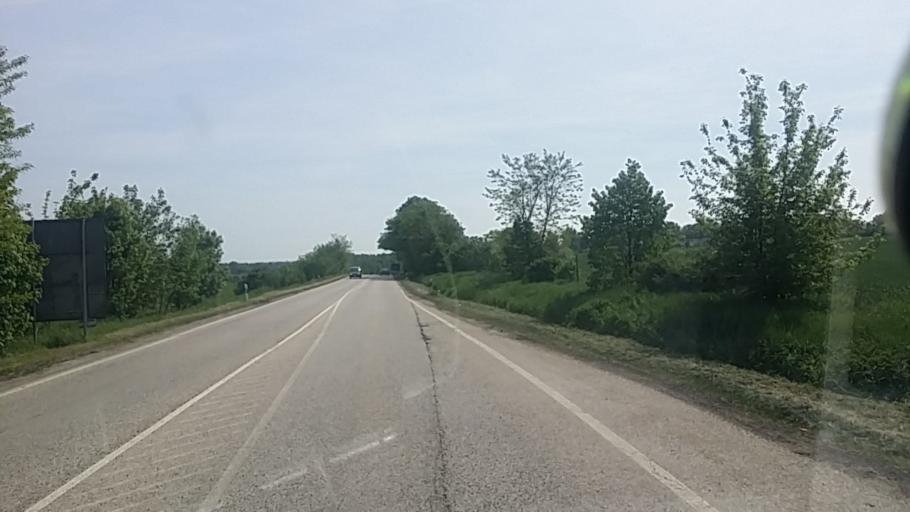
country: HU
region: Fejer
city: Etyek
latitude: 47.5031
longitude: 18.7600
